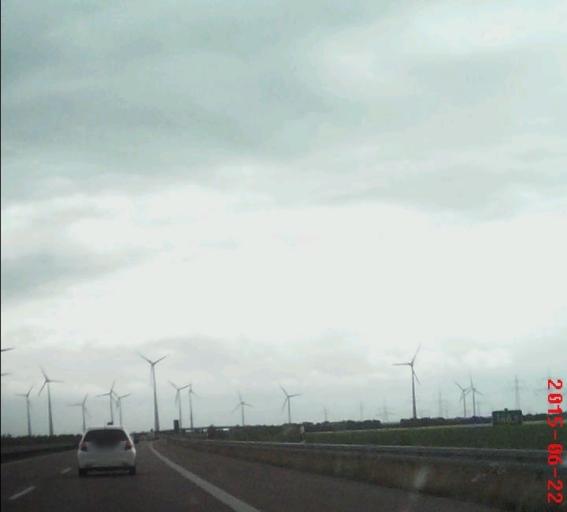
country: DE
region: Saxony-Anhalt
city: Schafstadt
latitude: 51.4000
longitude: 11.7532
